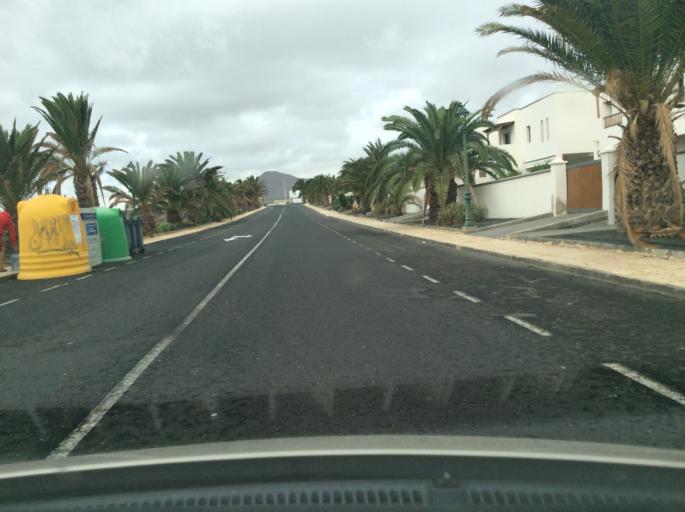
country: ES
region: Canary Islands
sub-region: Provincia de Las Palmas
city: Arrecife
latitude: 28.9849
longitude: -13.5148
